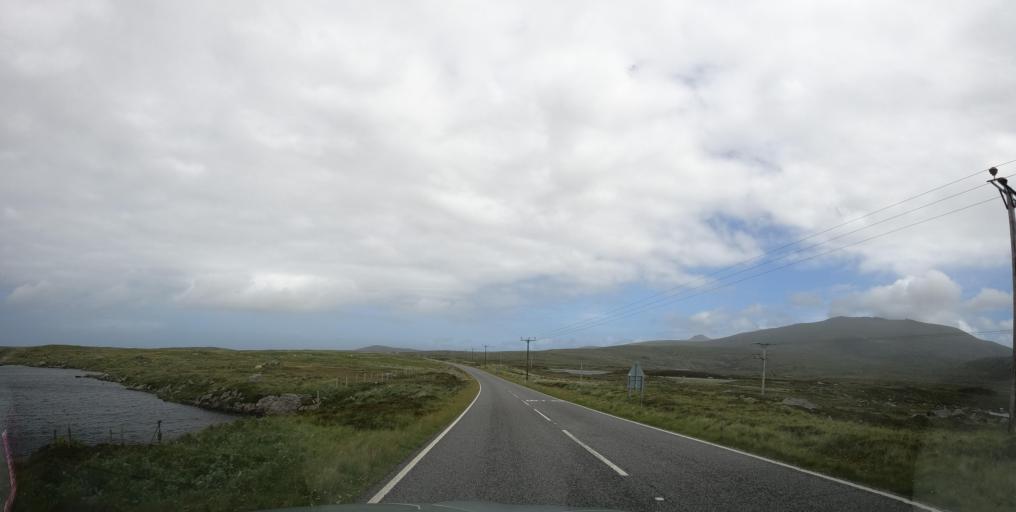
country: GB
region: Scotland
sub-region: Eilean Siar
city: Isle of South Uist
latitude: 57.2507
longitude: -7.3779
